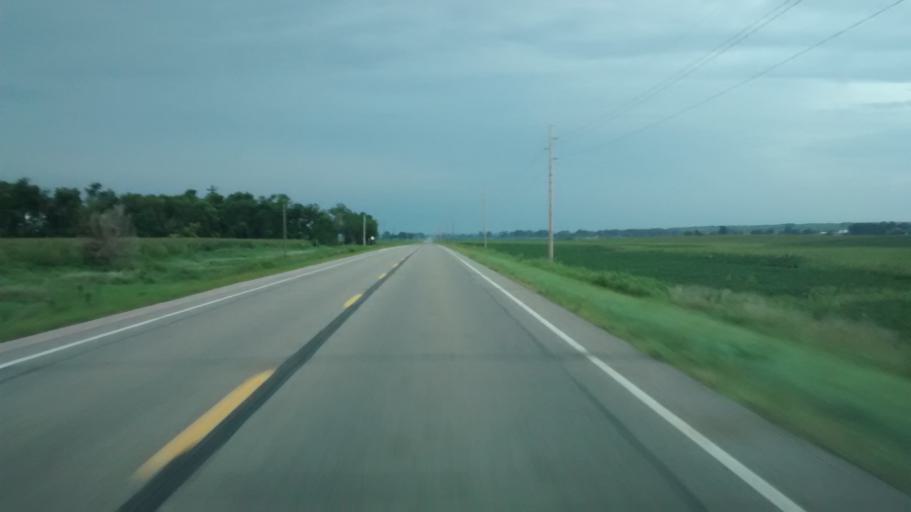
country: US
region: Iowa
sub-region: Plymouth County
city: Kingsley
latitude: 42.5550
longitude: -96.0161
